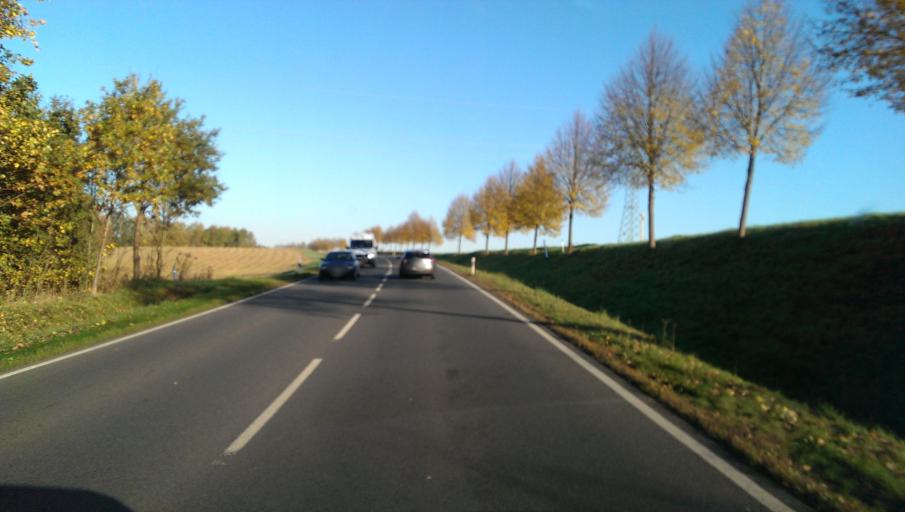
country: DE
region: Saxony
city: Niederwiesa
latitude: 50.8911
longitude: 12.9869
